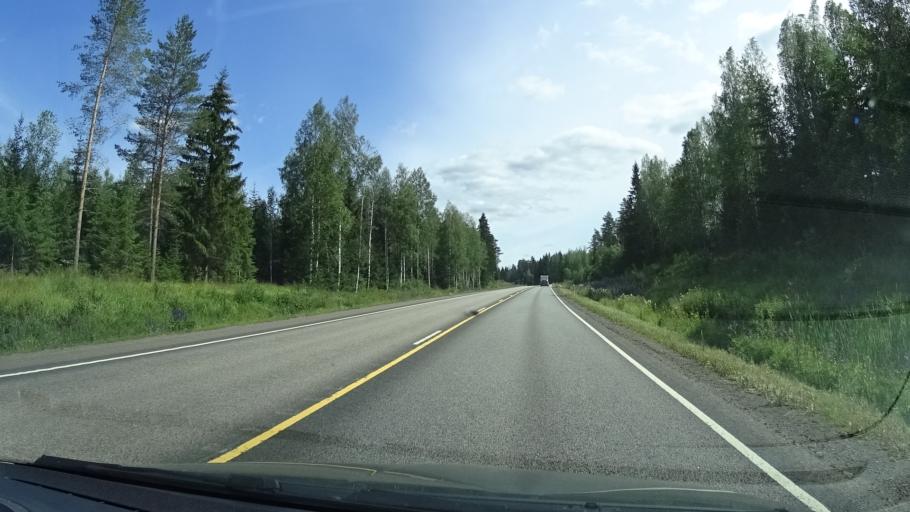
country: FI
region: Central Finland
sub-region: Jyvaeskylae
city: Muurame
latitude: 62.2670
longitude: 25.4943
